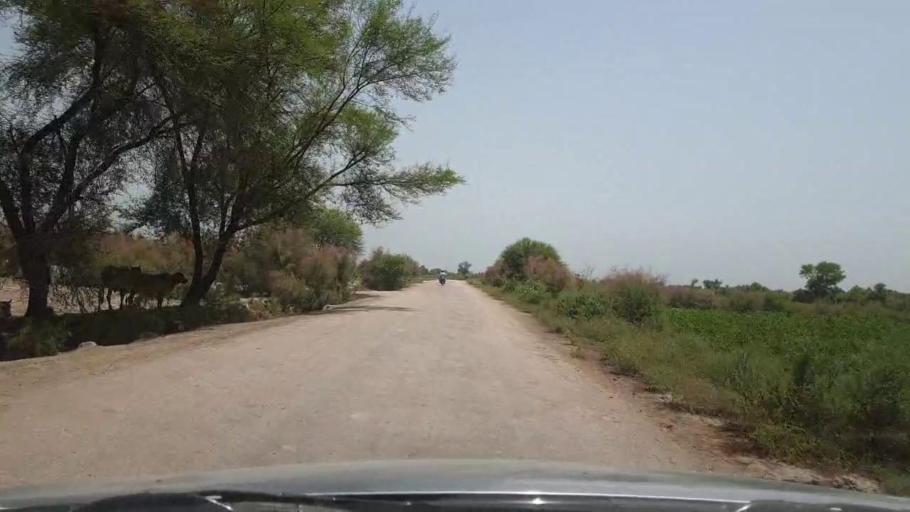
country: PK
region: Sindh
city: Pano Aqil
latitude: 27.8723
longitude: 69.1591
